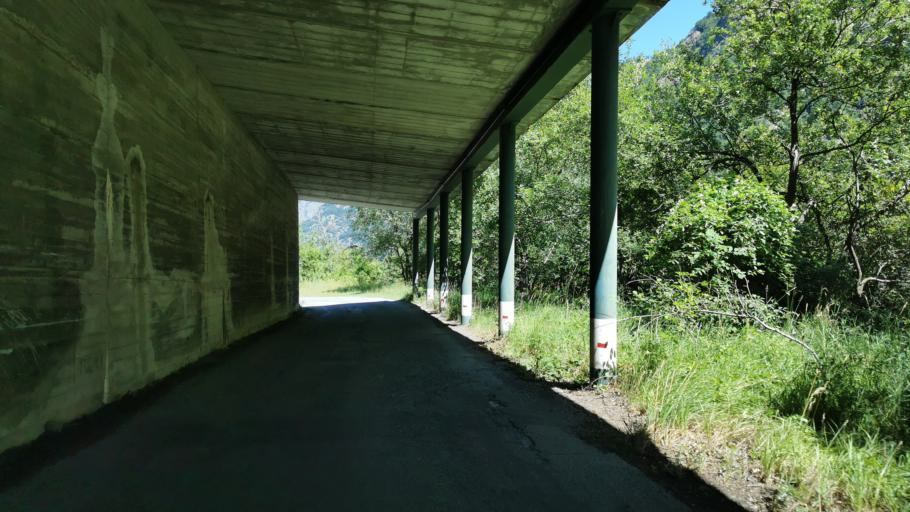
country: IT
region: Piedmont
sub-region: Provincia di Cuneo
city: Entracque
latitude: 44.1970
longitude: 7.3613
